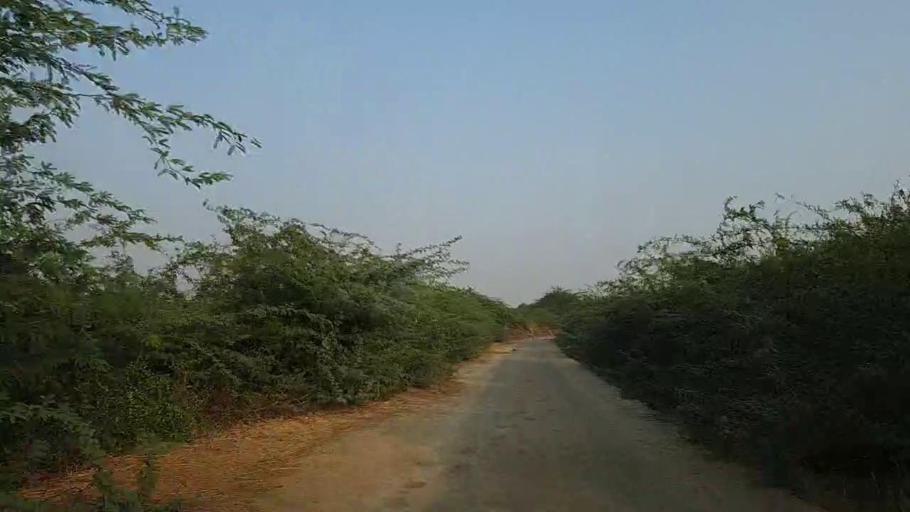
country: PK
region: Sindh
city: Thatta
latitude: 24.6898
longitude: 67.8172
